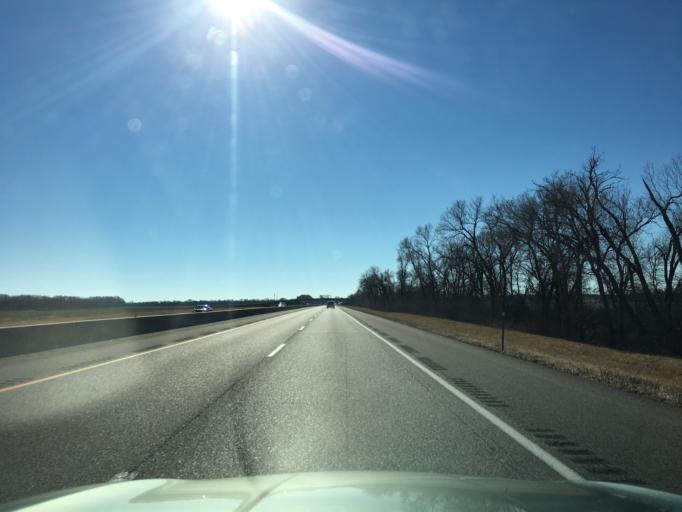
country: US
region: Kansas
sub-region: Sumner County
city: Belle Plaine
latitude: 37.4266
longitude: -97.3213
